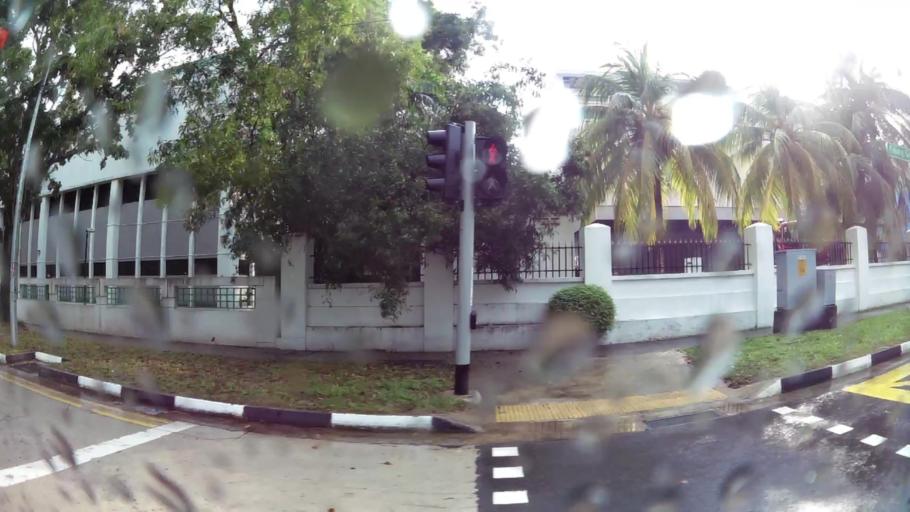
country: SG
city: Singapore
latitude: 1.3326
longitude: 103.9637
